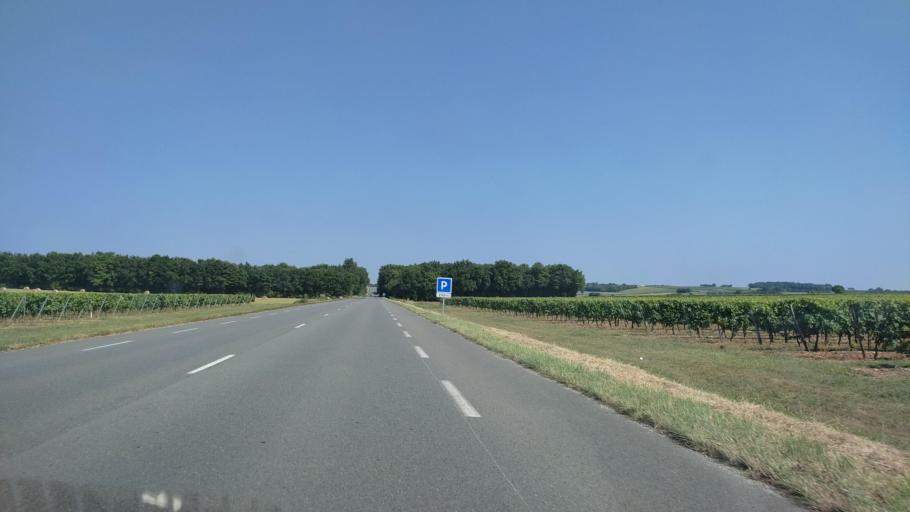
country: FR
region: Poitou-Charentes
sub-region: Departement de la Charente
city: Hiersac
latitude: 45.6741
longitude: -0.0220
